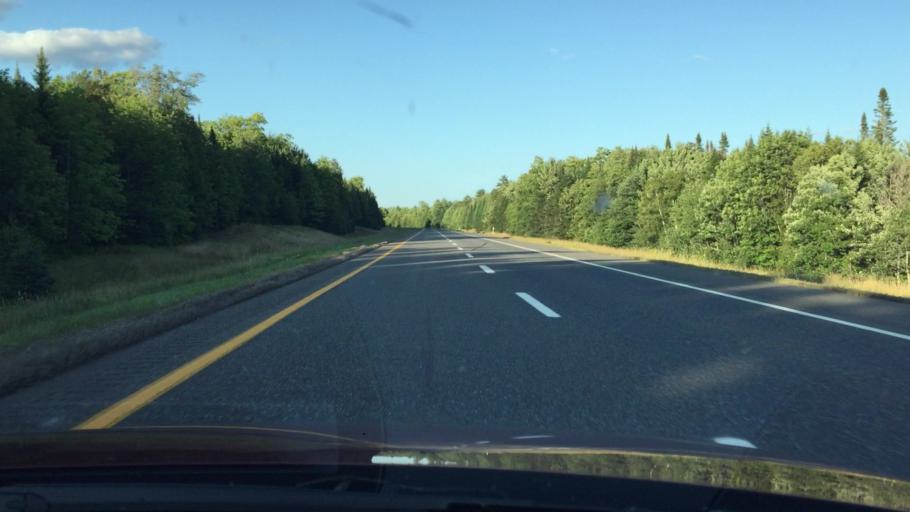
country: US
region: Maine
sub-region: Penobscot County
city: Patten
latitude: 46.0466
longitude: -68.2522
